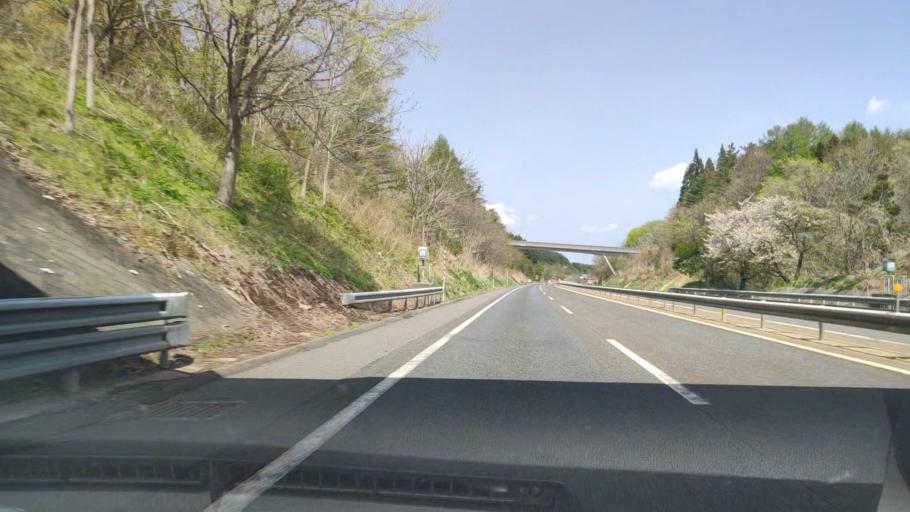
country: JP
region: Iwate
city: Ichinohe
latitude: 40.2605
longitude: 141.4011
